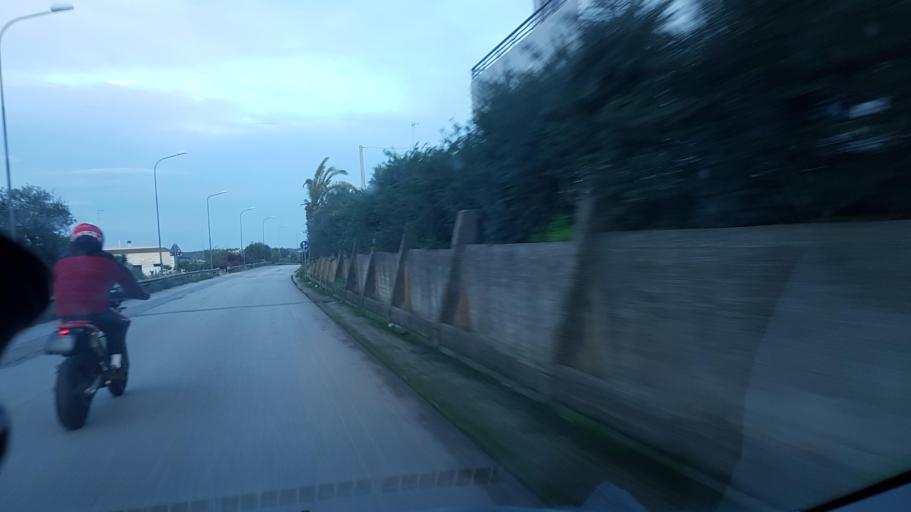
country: IT
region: Apulia
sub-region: Provincia di Brindisi
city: Ceglie Messapica
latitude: 40.6509
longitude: 17.5144
